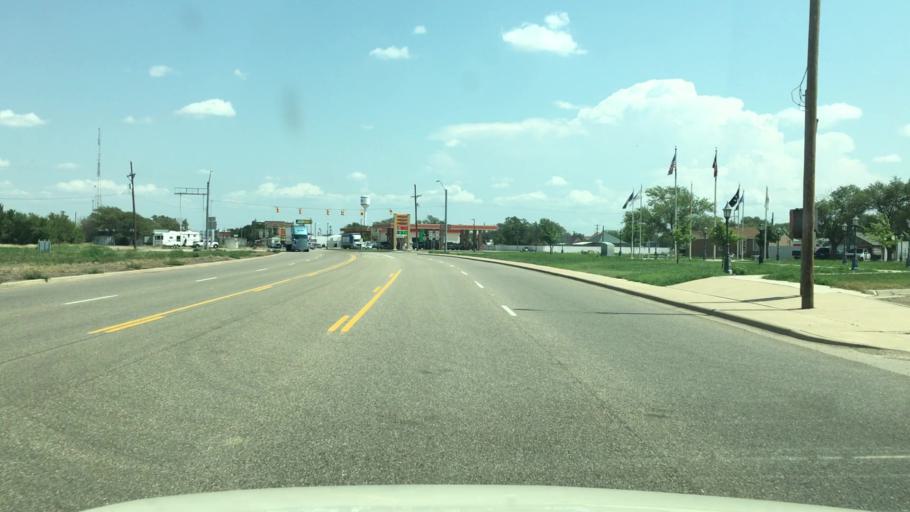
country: US
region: Texas
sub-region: Armstrong County
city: Claude
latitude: 35.1125
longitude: -101.3649
